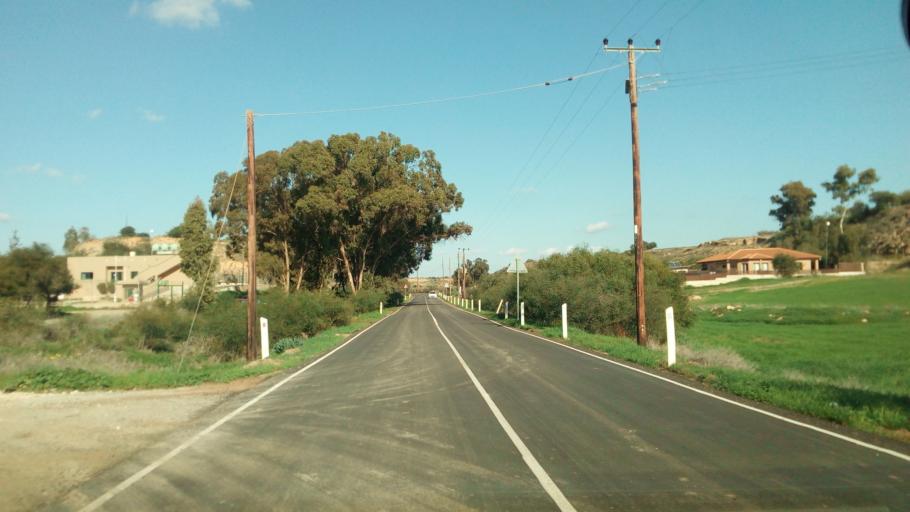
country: CY
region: Ammochostos
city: Avgorou
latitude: 35.0552
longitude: 33.8376
